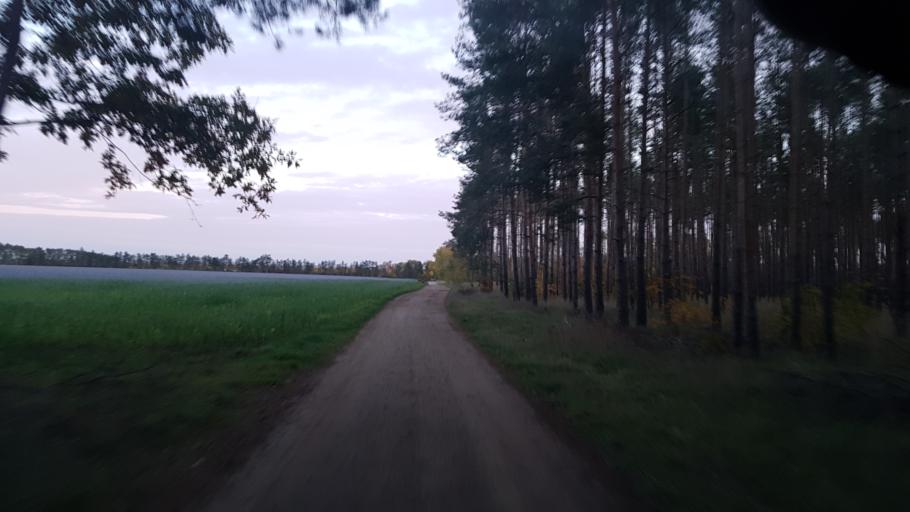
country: DE
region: Brandenburg
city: Bad Liebenwerda
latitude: 51.5079
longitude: 13.3191
